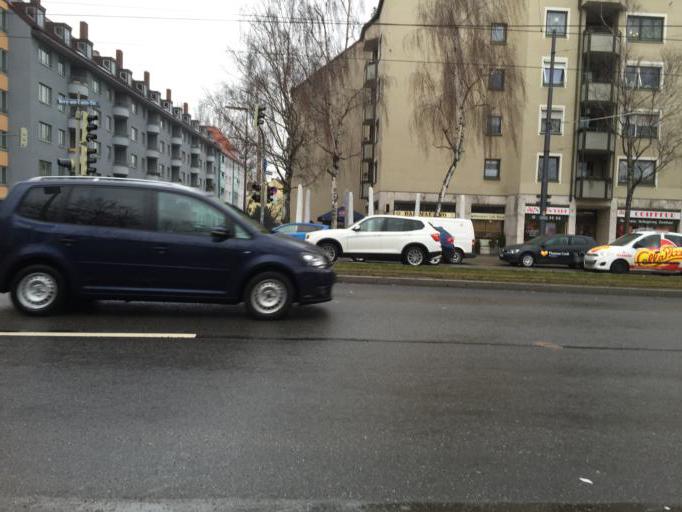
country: DE
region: Bavaria
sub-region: Upper Bavaria
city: Bogenhausen
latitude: 48.1306
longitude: 11.6173
